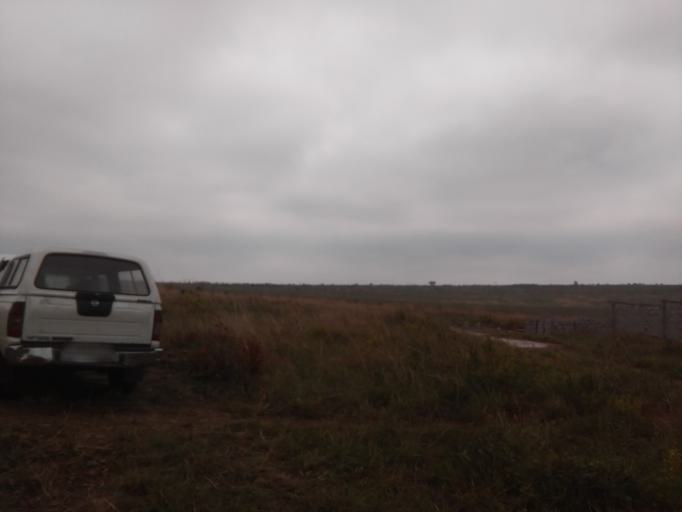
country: CD
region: Kinshasa
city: Masina
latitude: -4.4234
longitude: 15.9179
